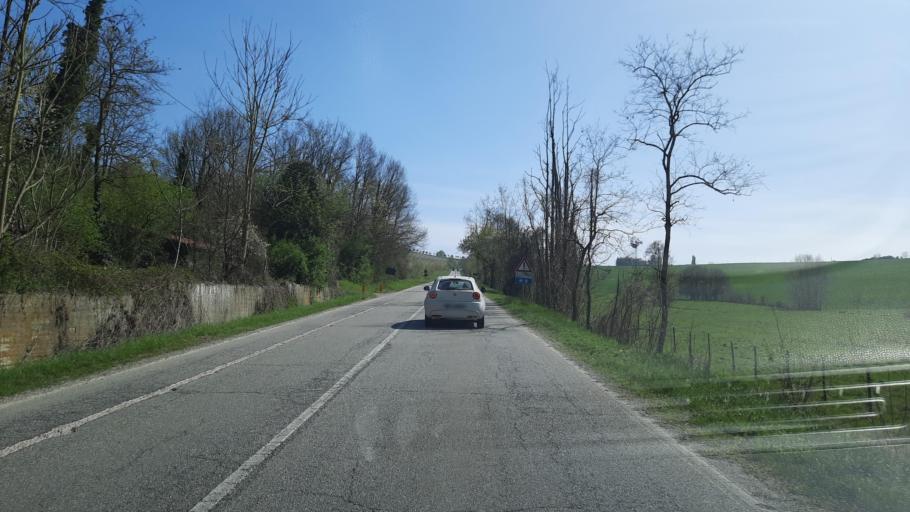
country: IT
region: Piedmont
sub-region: Provincia di Alessandria
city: Vignale Monferrato
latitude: 45.0174
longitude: 8.3884
